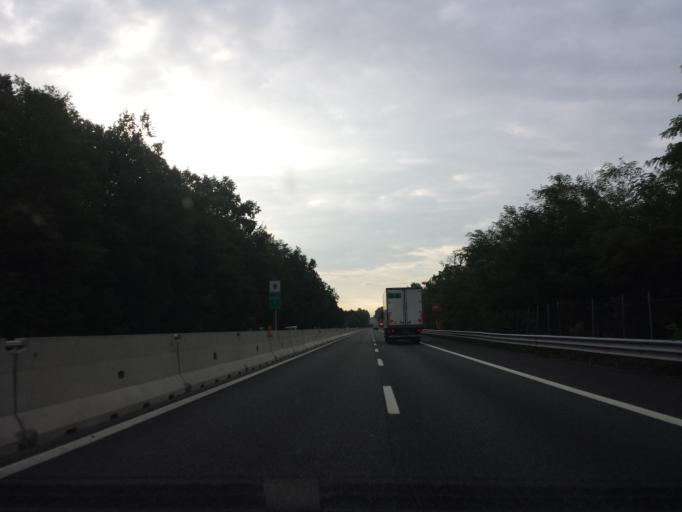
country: IT
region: Lombardy
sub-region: Provincia di Varese
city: Vergiate
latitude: 45.7173
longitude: 8.7042
